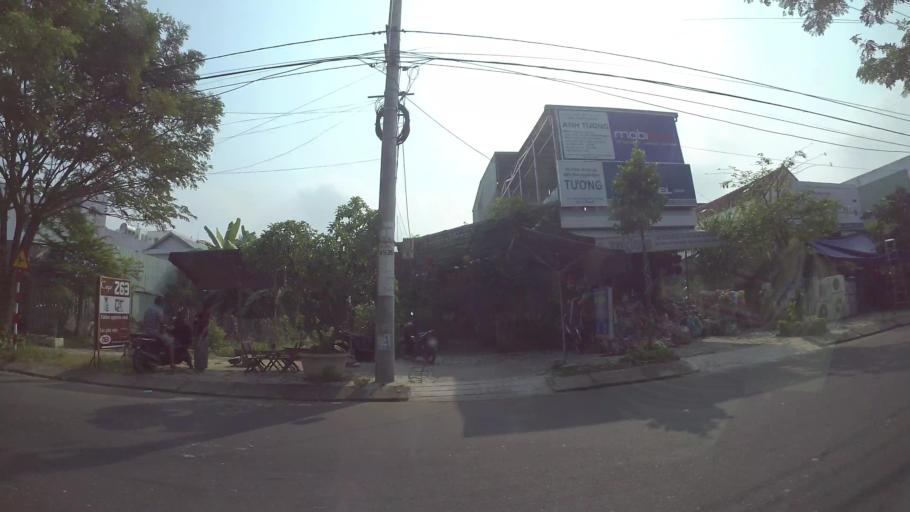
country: VN
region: Da Nang
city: Cam Le
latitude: 15.9975
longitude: 108.2133
